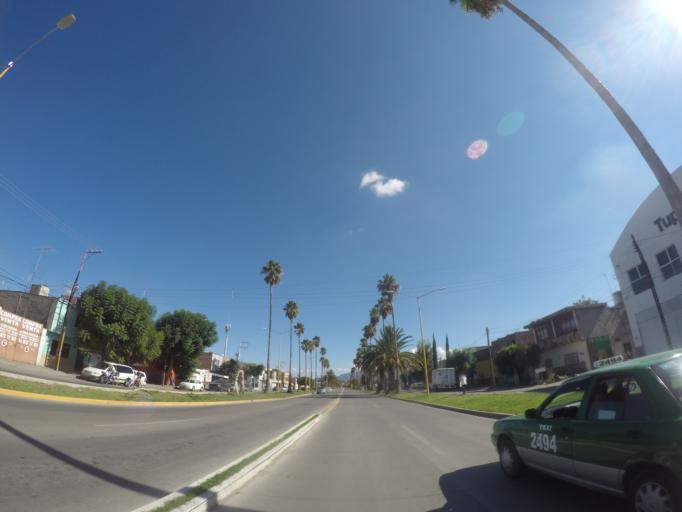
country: MX
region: San Luis Potosi
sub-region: San Luis Potosi
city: San Luis Potosi
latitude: 22.1674
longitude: -100.9725
